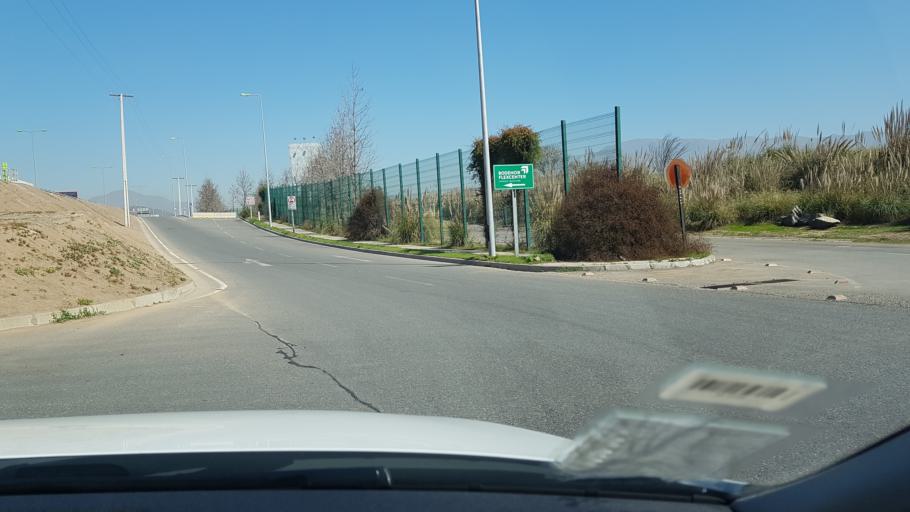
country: CL
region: Santiago Metropolitan
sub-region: Provincia de Santiago
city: Lo Prado
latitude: -33.4259
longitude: -70.8008
